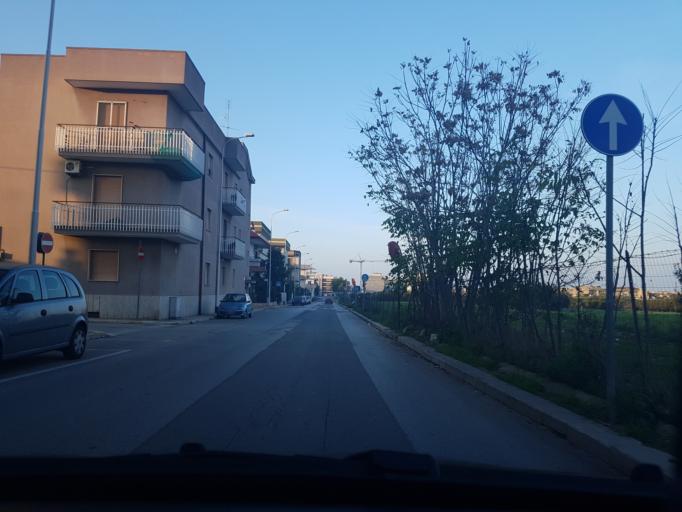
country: IT
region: Apulia
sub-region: Provincia di Bari
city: Bitritto
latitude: 41.0411
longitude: 16.8306
